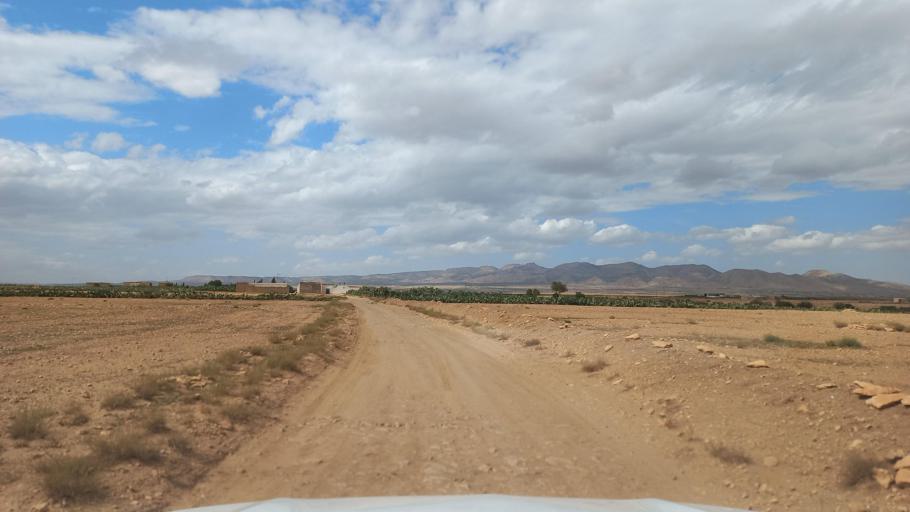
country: TN
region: Al Qasrayn
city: Sbiba
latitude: 35.3821
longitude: 9.0978
